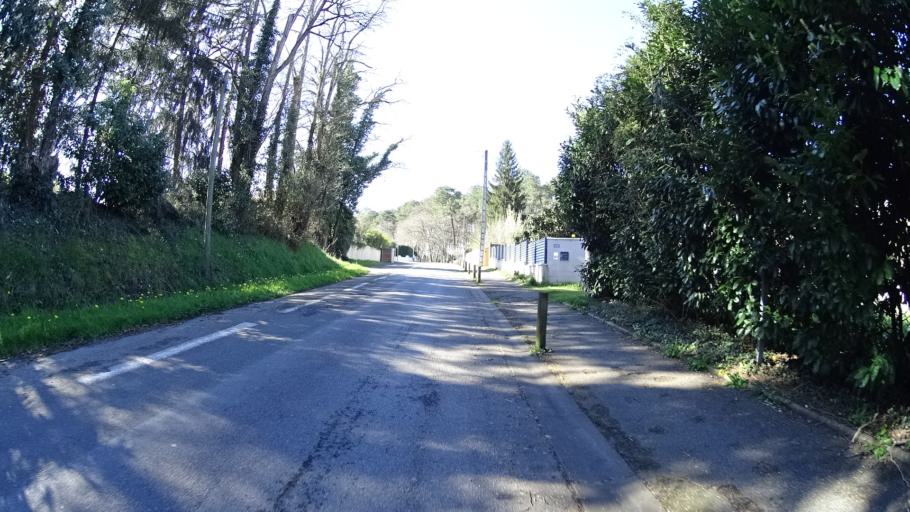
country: FR
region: Aquitaine
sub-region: Departement des Landes
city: Saint-Paul-les-Dax
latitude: 43.7335
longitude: -1.0744
